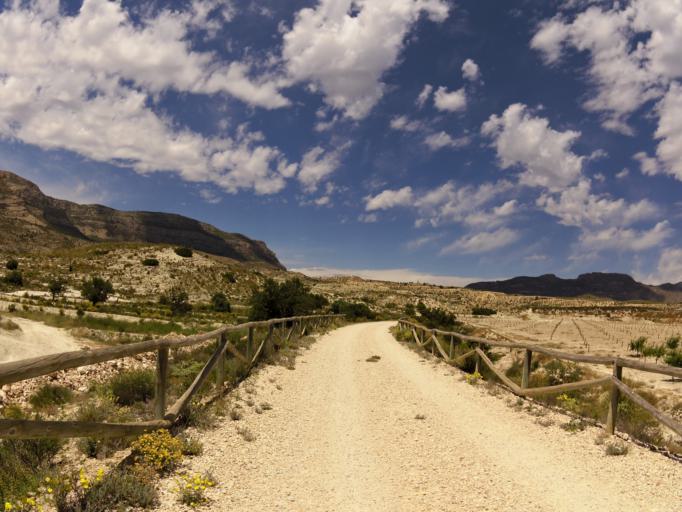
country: ES
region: Valencia
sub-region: Provincia de Alicante
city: Agost
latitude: 38.4456
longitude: -0.6865
